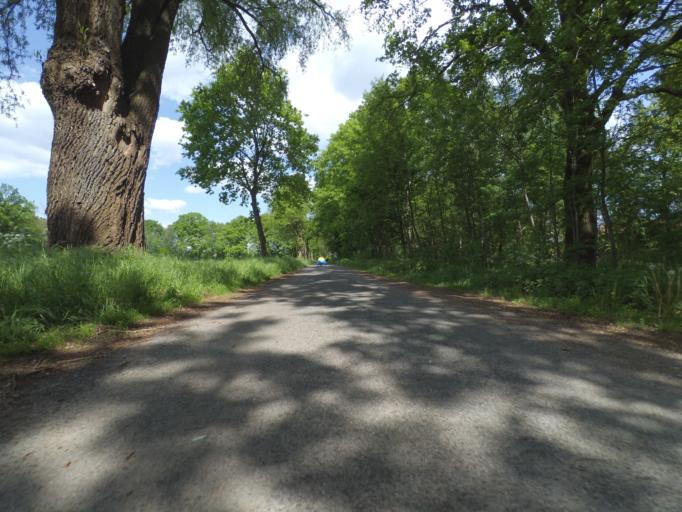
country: DE
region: Lower Saxony
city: Meinersen
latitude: 52.4588
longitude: 10.3224
